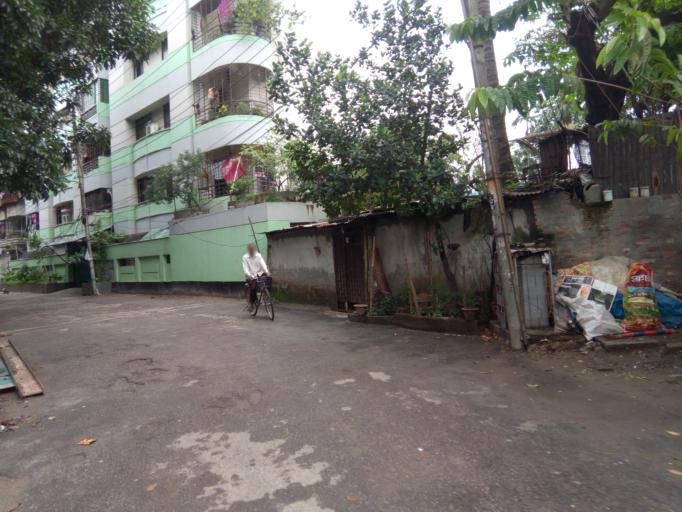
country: BD
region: Dhaka
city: Azimpur
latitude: 23.7584
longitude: 90.3686
